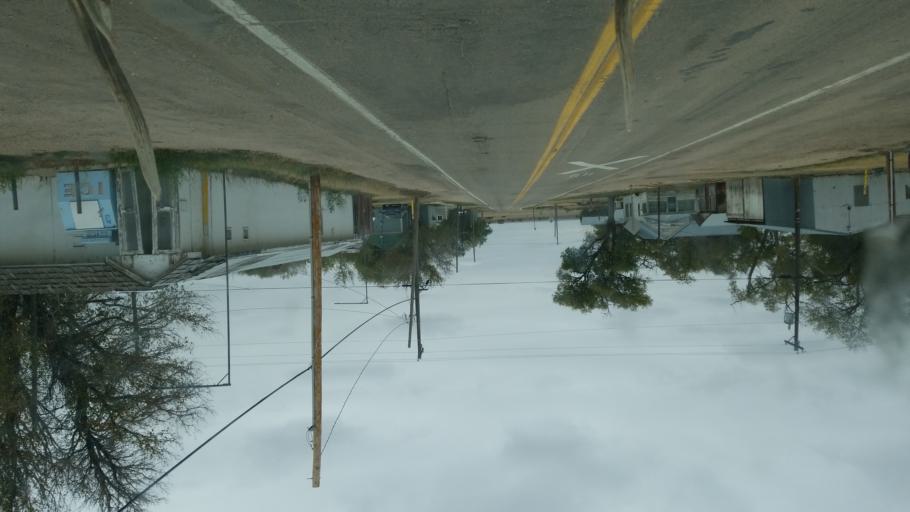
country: US
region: Colorado
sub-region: Crowley County
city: Ordway
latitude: 38.2333
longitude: -103.6628
